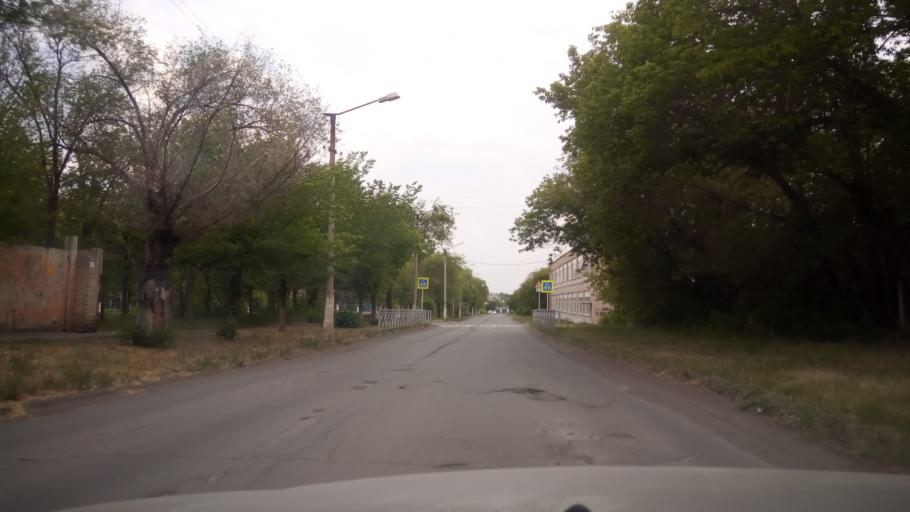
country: RU
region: Orenburg
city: Novotroitsk
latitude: 51.2032
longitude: 58.3060
